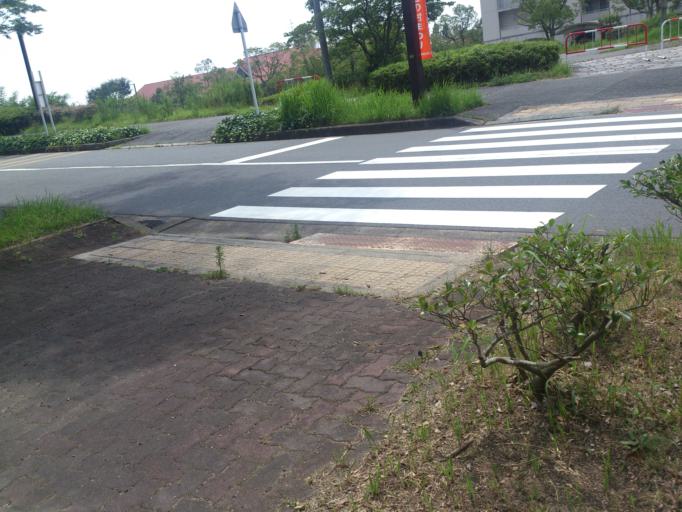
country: JP
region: Hyogo
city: Kobe
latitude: 34.7055
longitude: 135.1163
